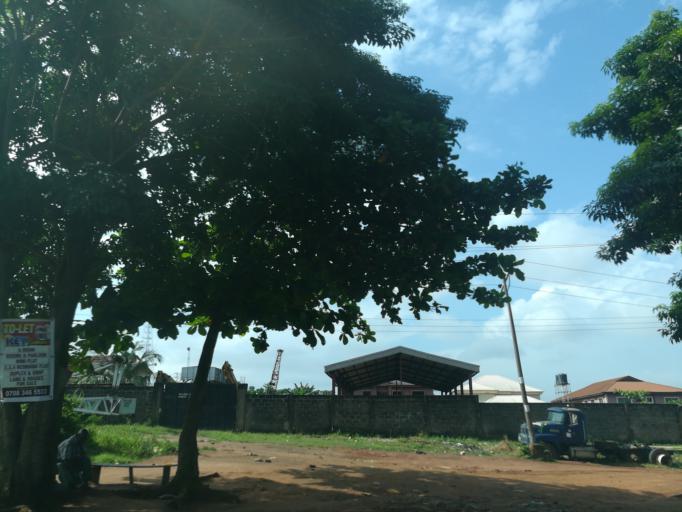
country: NG
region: Lagos
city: Ikorodu
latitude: 6.6303
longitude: 3.5187
